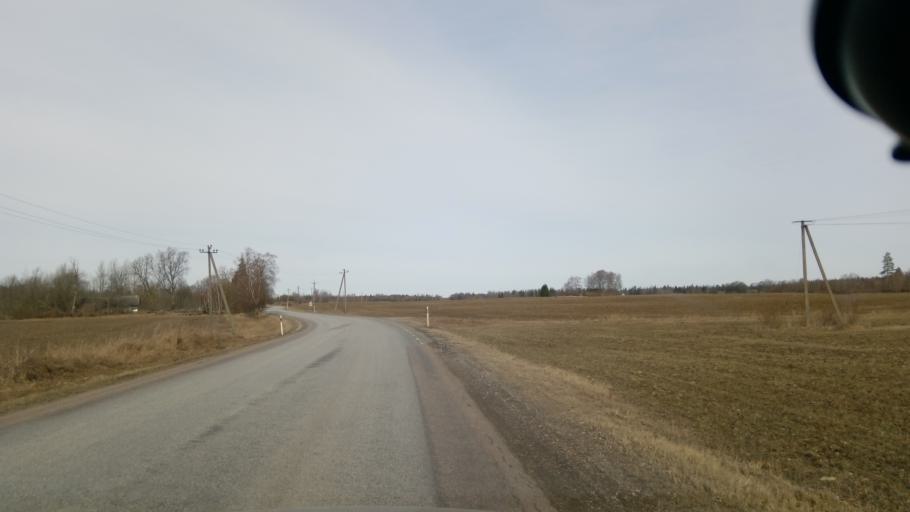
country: EE
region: Raplamaa
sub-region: Rapla vald
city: Rapla
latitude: 59.0276
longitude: 24.8382
